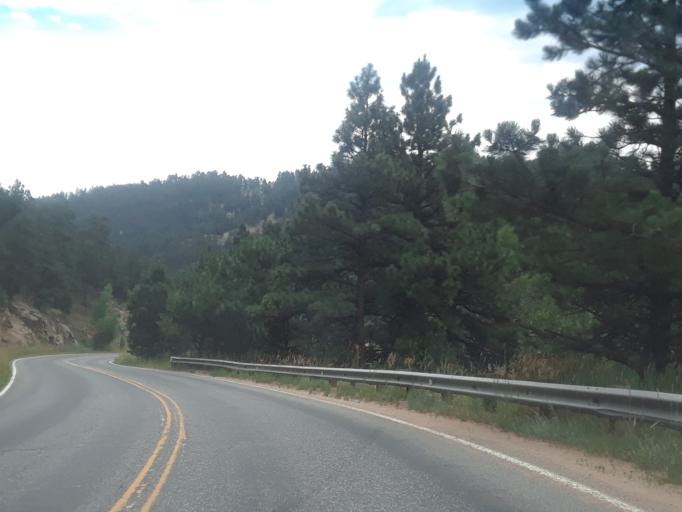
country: US
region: Colorado
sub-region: Boulder County
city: Boulder
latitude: 40.0302
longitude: -105.3155
